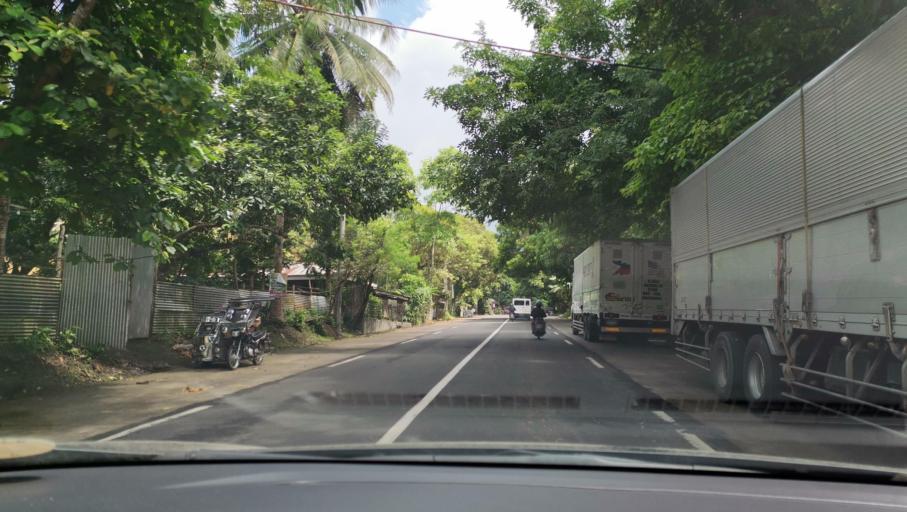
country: PH
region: Calabarzon
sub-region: Province of Quezon
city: Calauag
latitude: 13.9520
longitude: 122.2887
